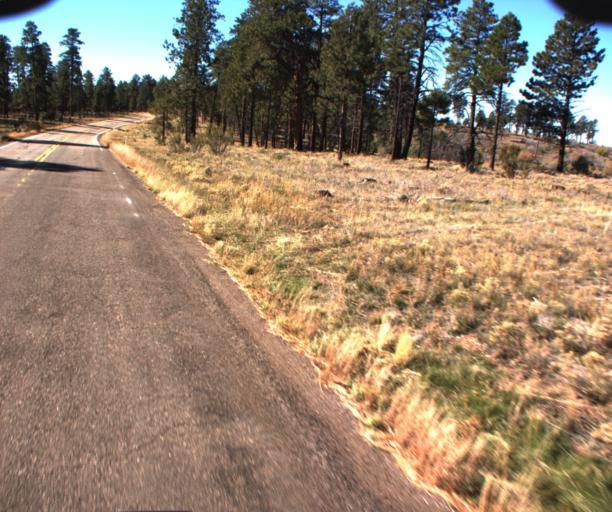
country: US
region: Arizona
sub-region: Coconino County
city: Fredonia
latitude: 36.7660
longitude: -112.2580
